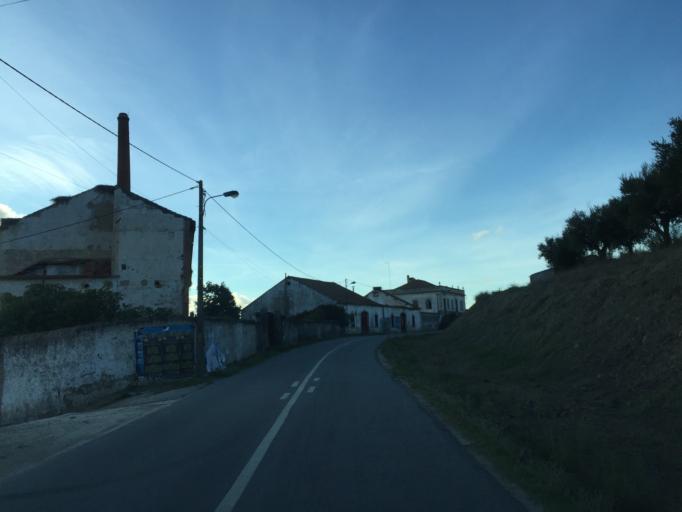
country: PT
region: Portalegre
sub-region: Alter do Chao
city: Alter do Chao
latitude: 39.2820
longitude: -7.6443
